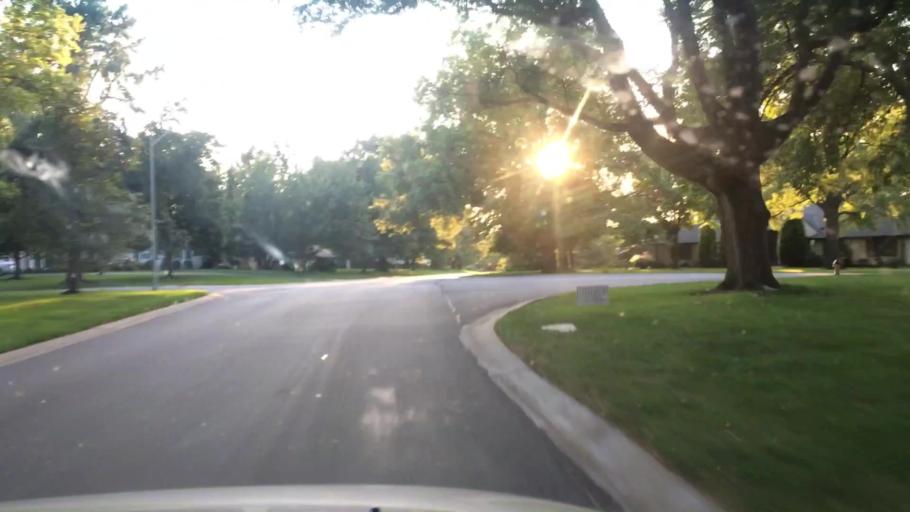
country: US
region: Kansas
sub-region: Johnson County
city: Leawood
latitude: 38.9677
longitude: -94.6332
